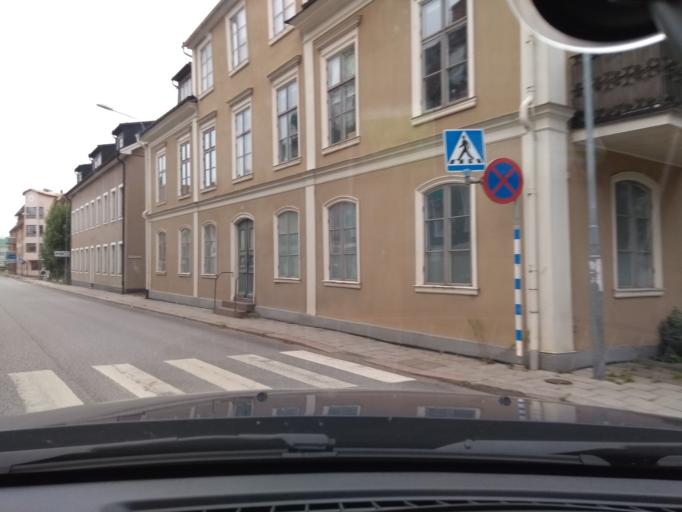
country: SE
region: Joenkoeping
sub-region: Eksjo Kommun
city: Eksjoe
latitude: 57.6663
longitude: 14.9699
